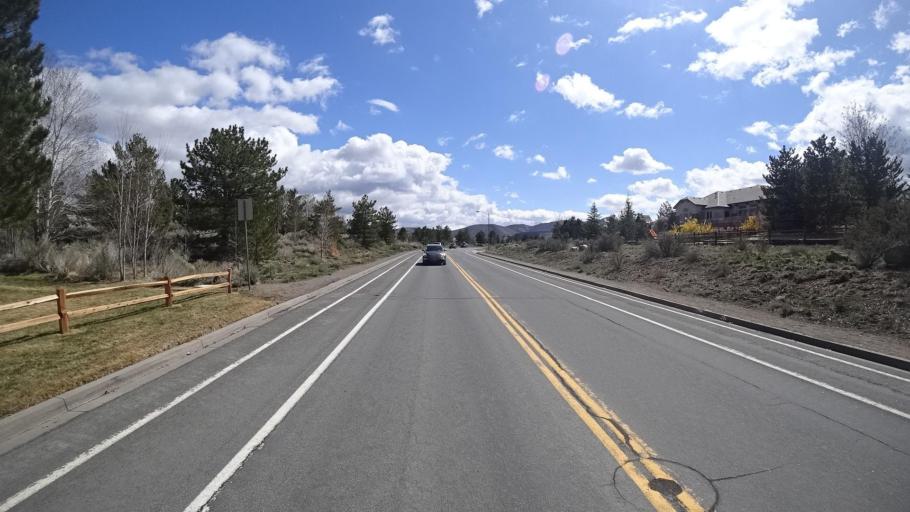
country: US
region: Nevada
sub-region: Washoe County
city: Reno
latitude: 39.3982
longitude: -119.7928
